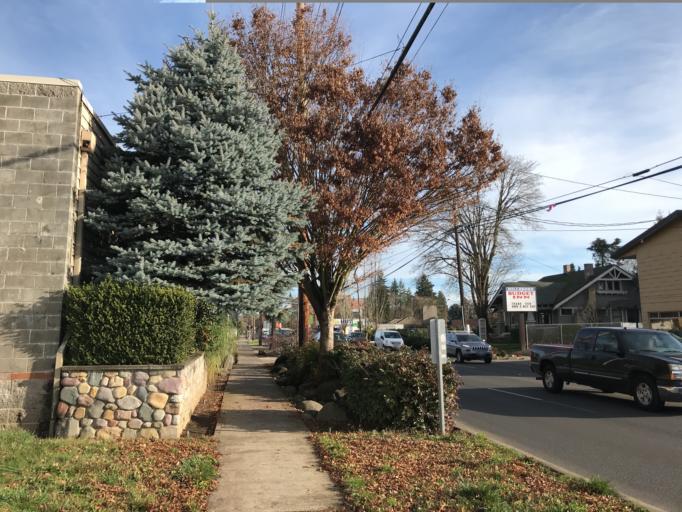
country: US
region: Oregon
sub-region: Washington County
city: Hillsboro
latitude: 45.5201
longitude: -122.9840
